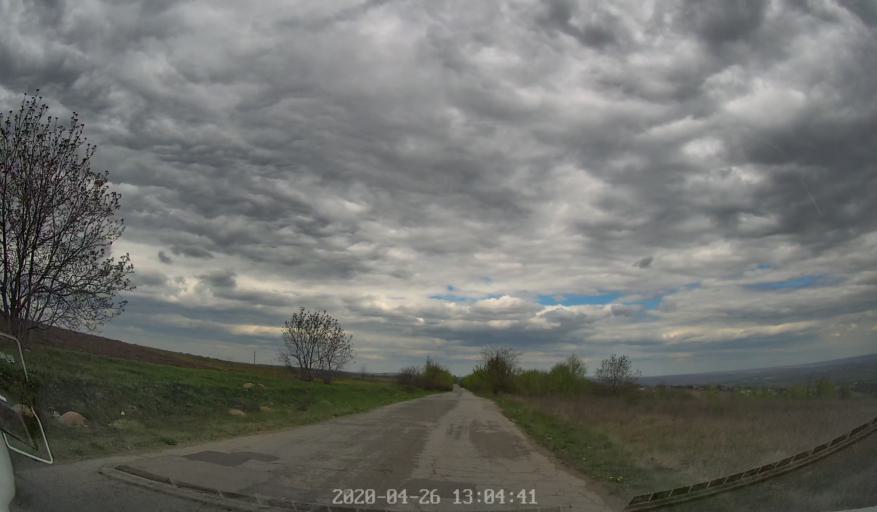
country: MD
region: Chisinau
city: Vadul lui Voda
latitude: 47.0704
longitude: 29.0675
